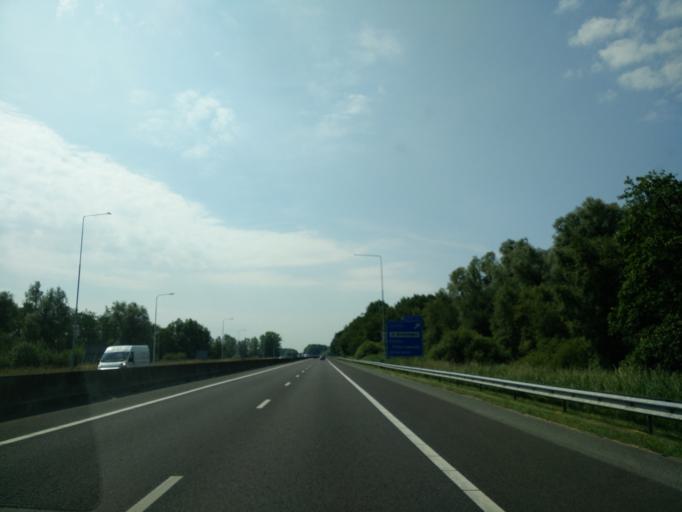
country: NL
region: Groningen
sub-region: Gemeente Haren
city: Haren
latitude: 53.1391
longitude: 6.6081
